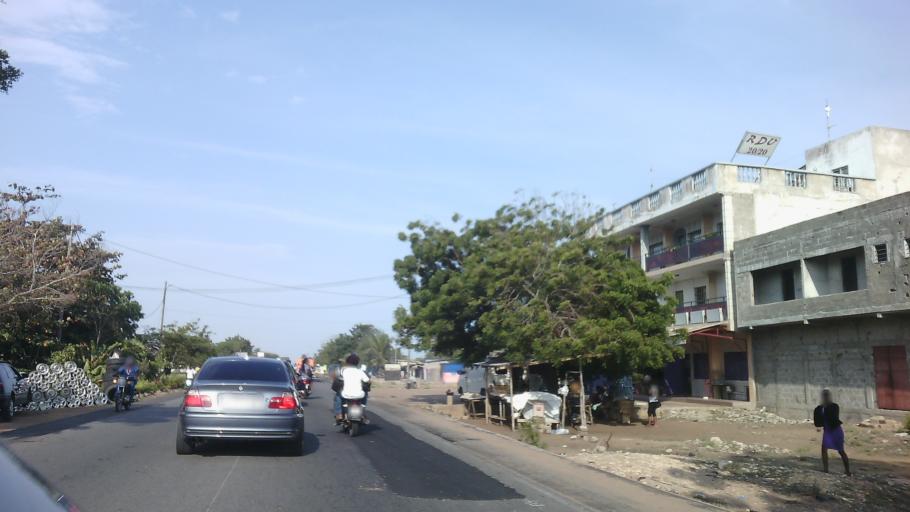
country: TG
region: Maritime
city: Lome
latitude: 6.1767
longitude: 1.3687
